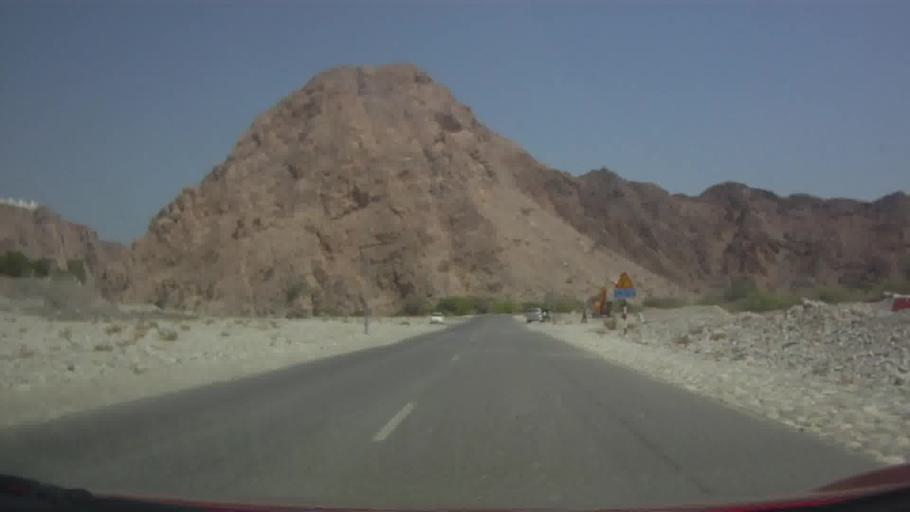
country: OM
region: Muhafazat Masqat
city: Muscat
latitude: 23.5109
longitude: 58.6461
